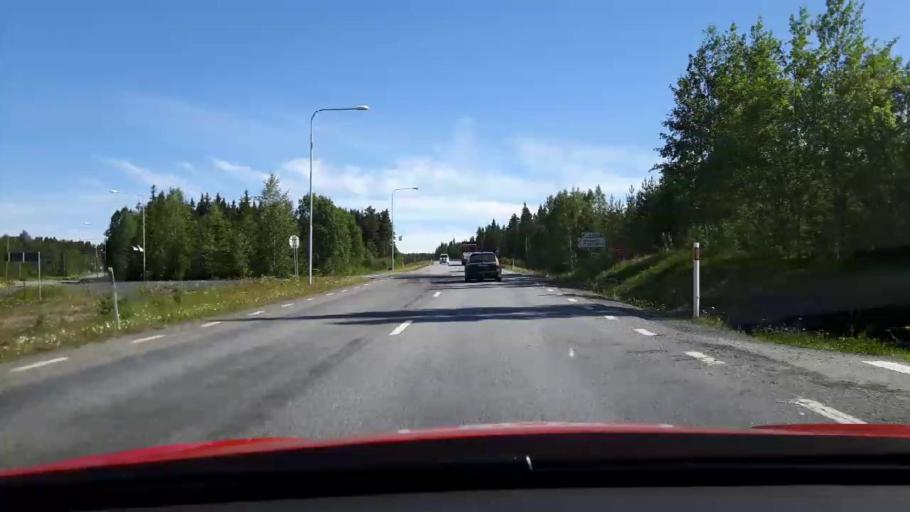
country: SE
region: Jaemtland
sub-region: OEstersunds Kommun
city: Lit
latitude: 63.3798
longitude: 14.8877
